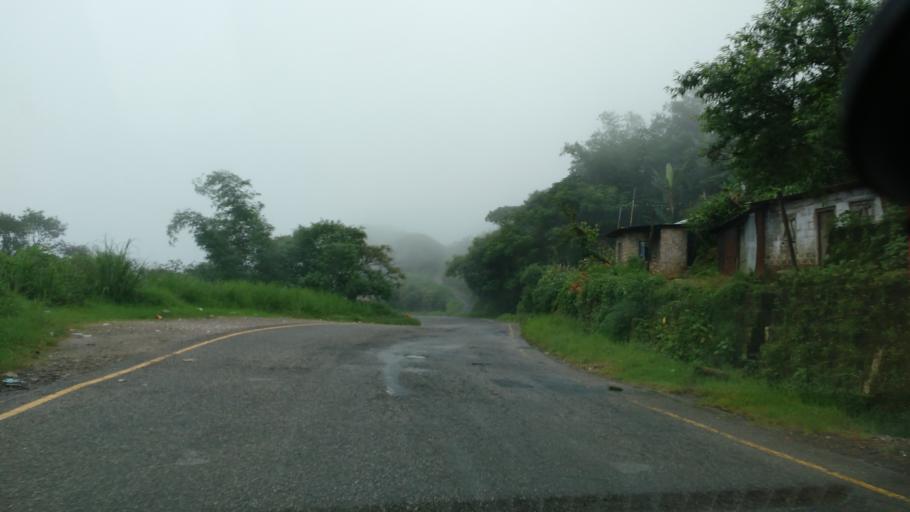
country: IN
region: Meghalaya
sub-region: East Khasi Hills
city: Cherrapunji
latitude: 25.2861
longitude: 91.7239
